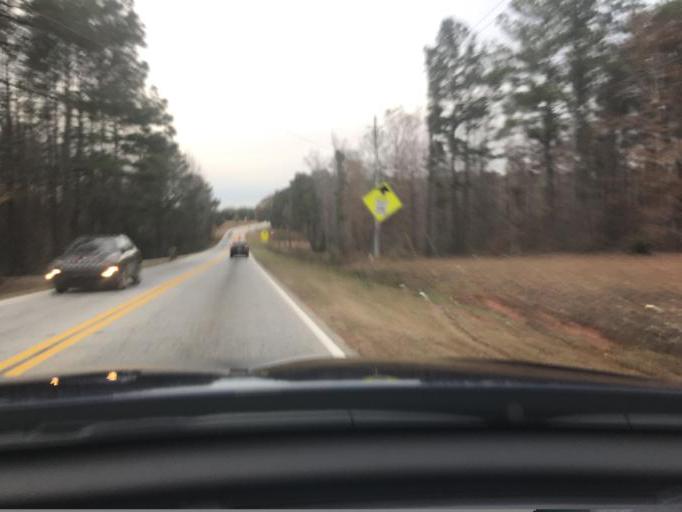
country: US
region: Georgia
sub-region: Newton County
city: Porterdale
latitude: 33.5943
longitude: -83.9146
